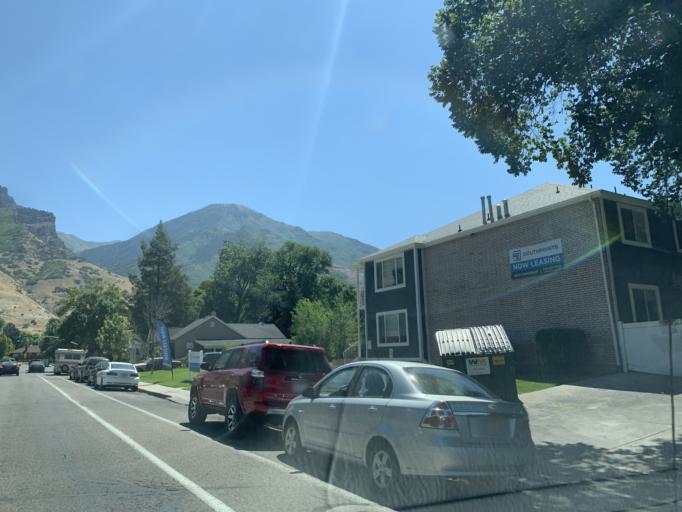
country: US
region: Utah
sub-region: Utah County
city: Provo
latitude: 40.2297
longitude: -111.6442
